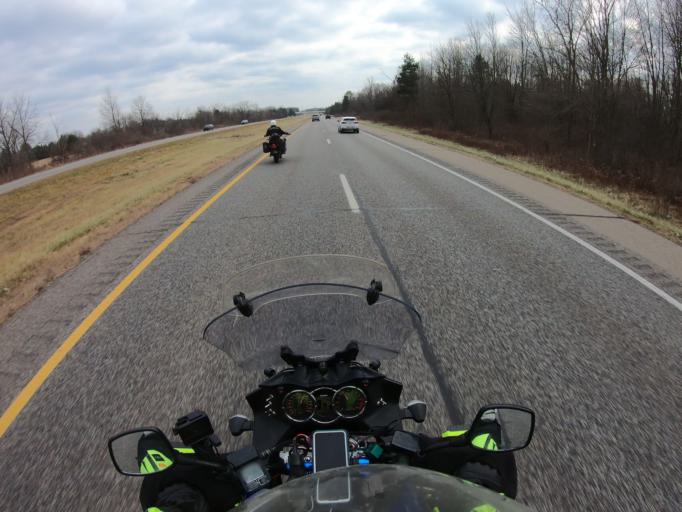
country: US
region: Michigan
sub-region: Genesee County
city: Grand Blanc
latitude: 42.9316
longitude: -83.6990
